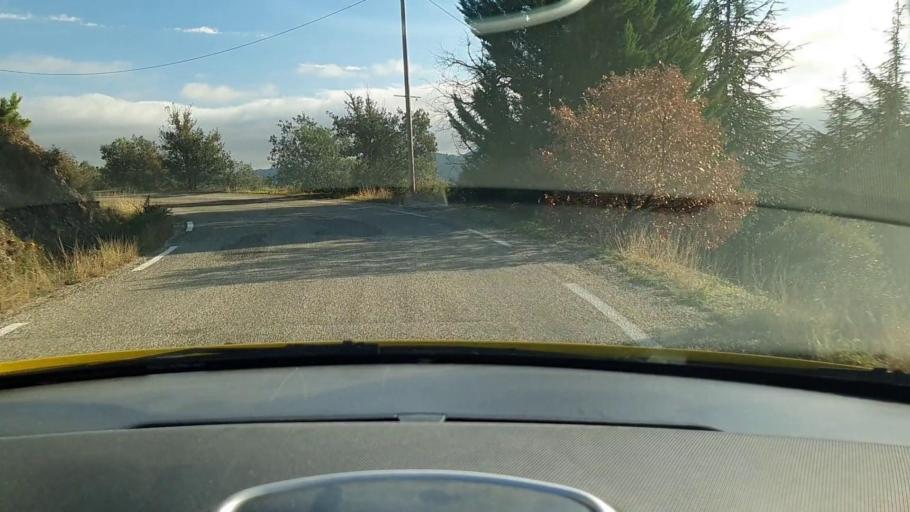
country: FR
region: Languedoc-Roussillon
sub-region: Departement du Gard
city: Branoux-les-Taillades
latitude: 44.3121
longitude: 3.9975
